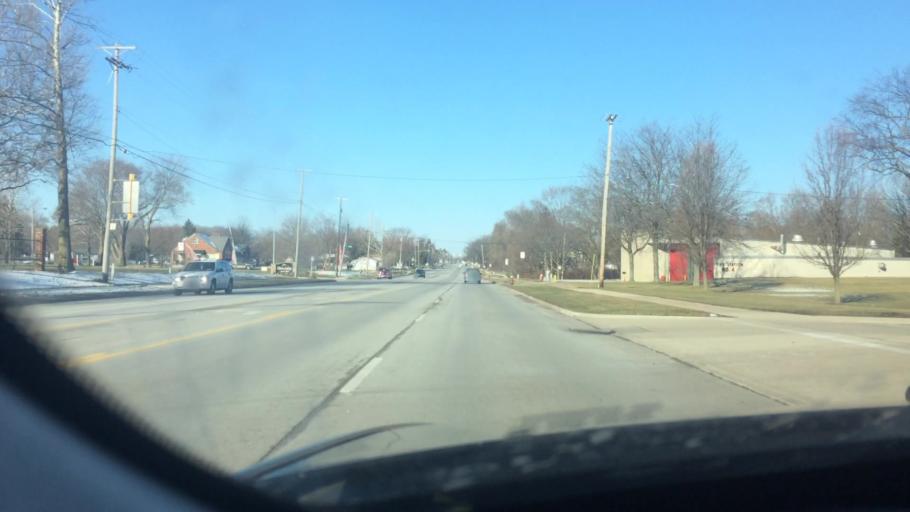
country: US
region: Ohio
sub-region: Lucas County
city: Ottawa Hills
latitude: 41.6383
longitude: -83.6339
